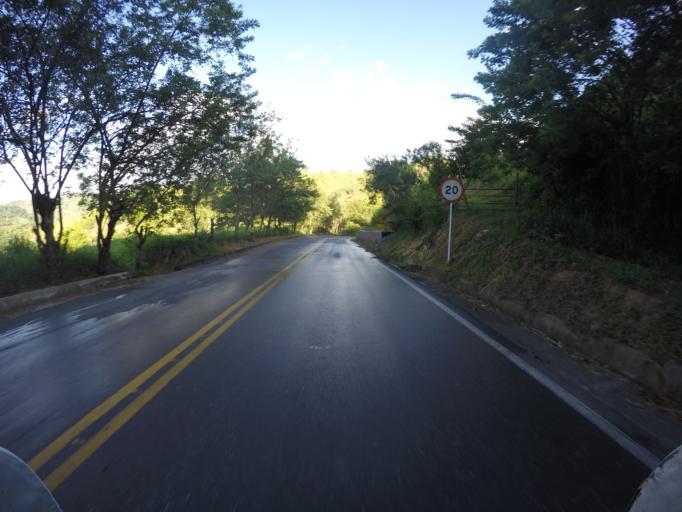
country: CO
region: Valle del Cauca
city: Cartago
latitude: 4.7187
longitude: -75.8620
